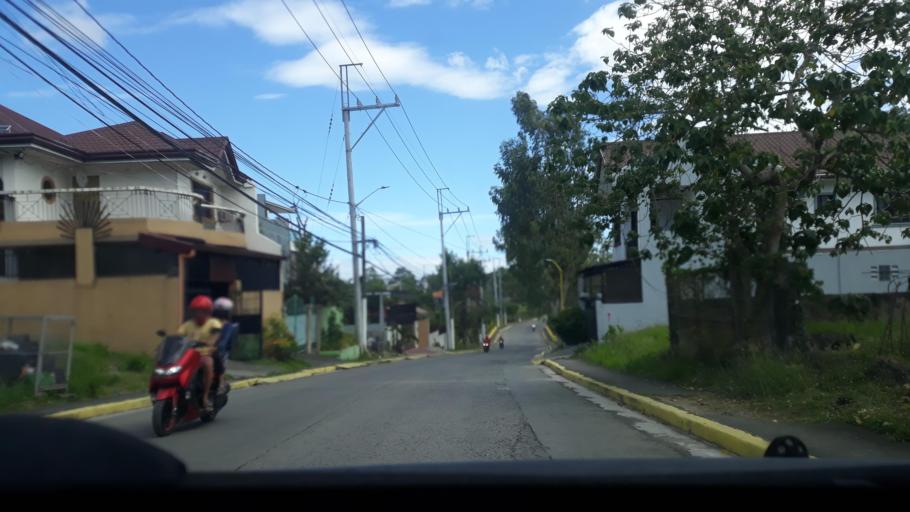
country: PH
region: Calabarzon
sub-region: Province of Cavite
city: Bulihan
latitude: 14.3024
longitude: 120.9663
